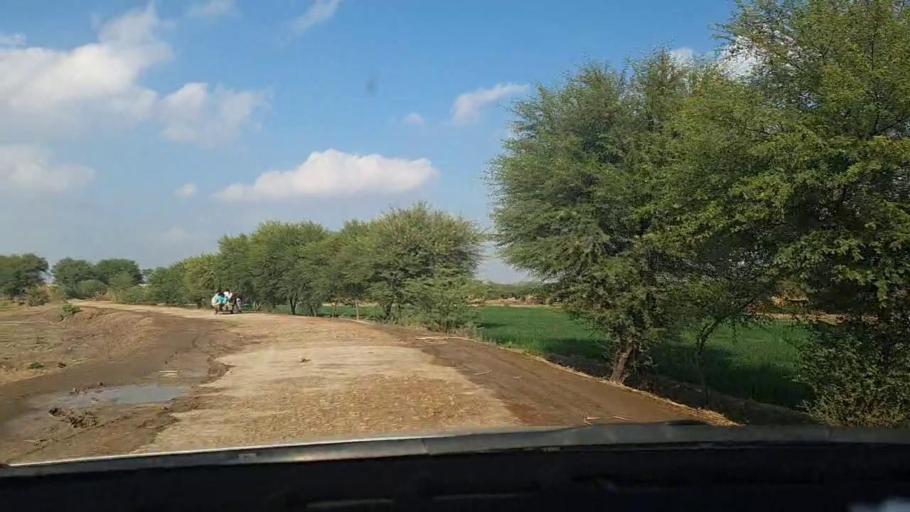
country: PK
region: Sindh
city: Tando Mittha Khan
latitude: 25.8744
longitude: 69.2928
